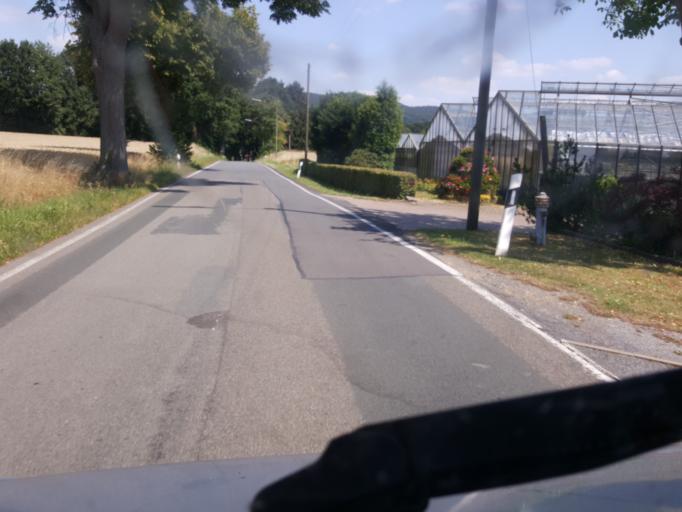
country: DE
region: North Rhine-Westphalia
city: Bad Oeynhausen
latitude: 52.2581
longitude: 8.7547
